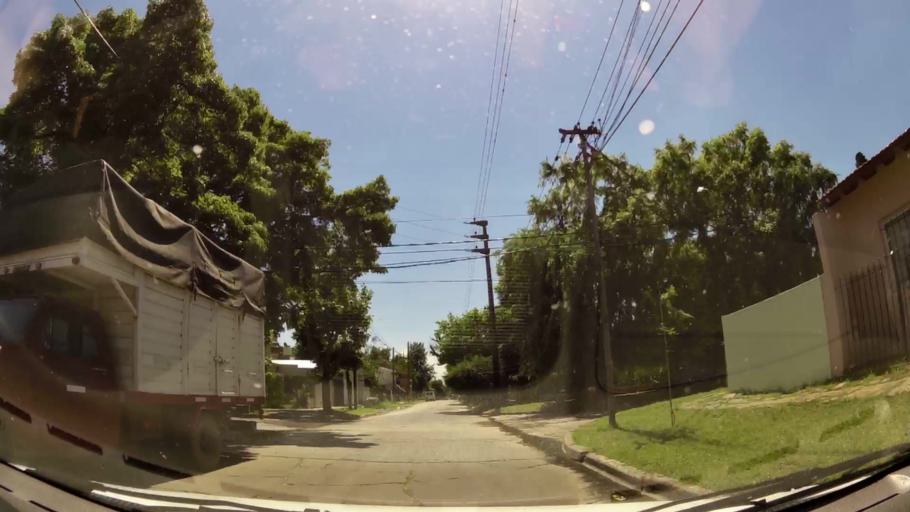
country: AR
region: Buenos Aires
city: Ituzaingo
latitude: -34.6618
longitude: -58.6822
